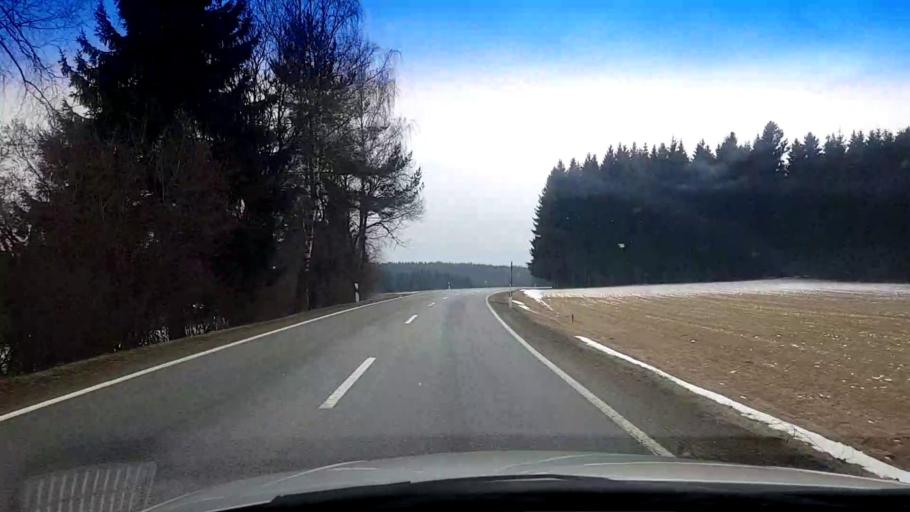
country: DE
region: Bavaria
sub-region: Upper Franconia
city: Stammbach
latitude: 50.1817
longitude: 11.7017
